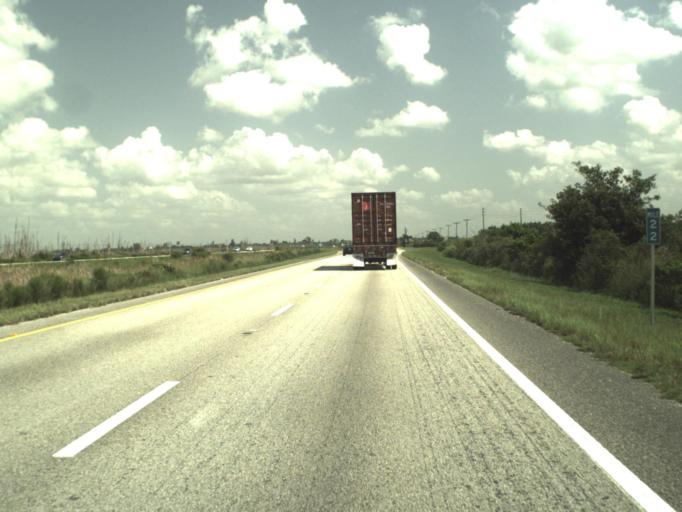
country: US
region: Florida
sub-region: Miami-Dade County
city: Palm Springs North
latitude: 25.9903
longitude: -80.4318
